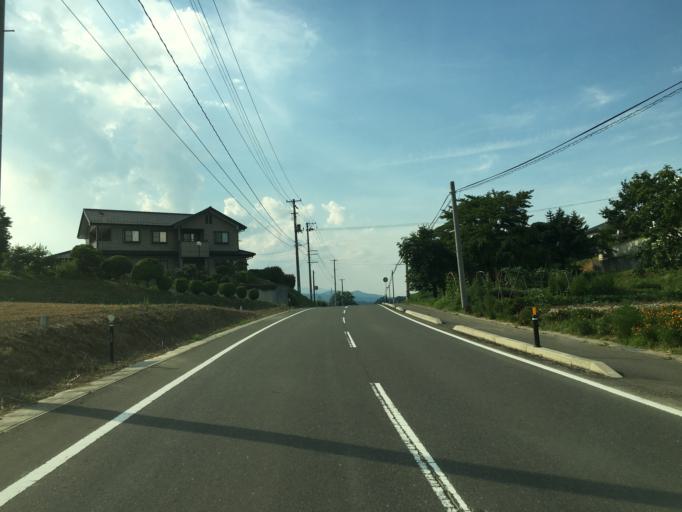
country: JP
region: Fukushima
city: Nihommatsu
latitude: 37.5563
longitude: 140.4315
